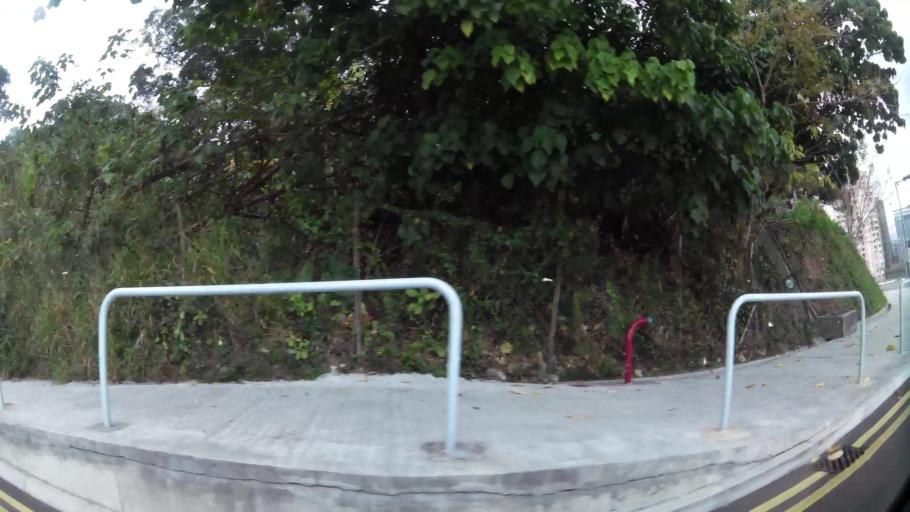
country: HK
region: Kowloon City
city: Kowloon
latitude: 22.3091
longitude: 114.1814
